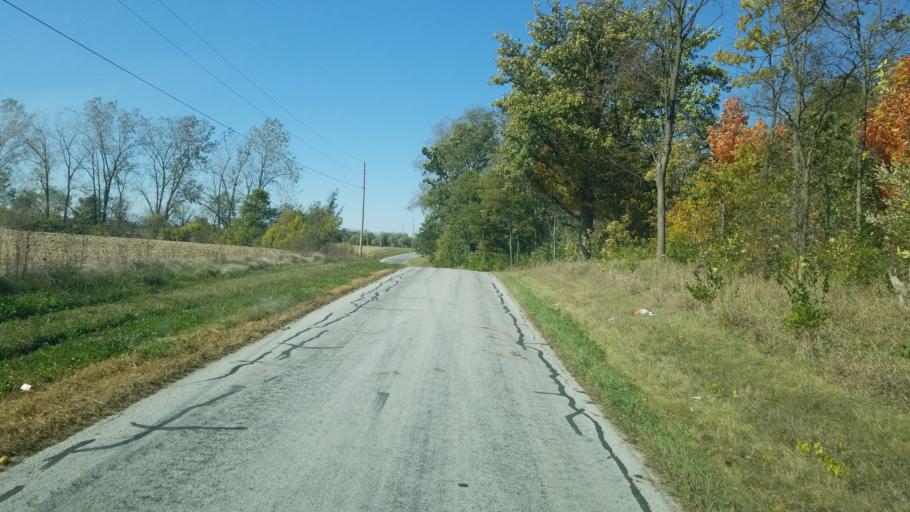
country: US
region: Ohio
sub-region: Hardin County
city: Kenton
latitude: 40.6345
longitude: -83.5703
